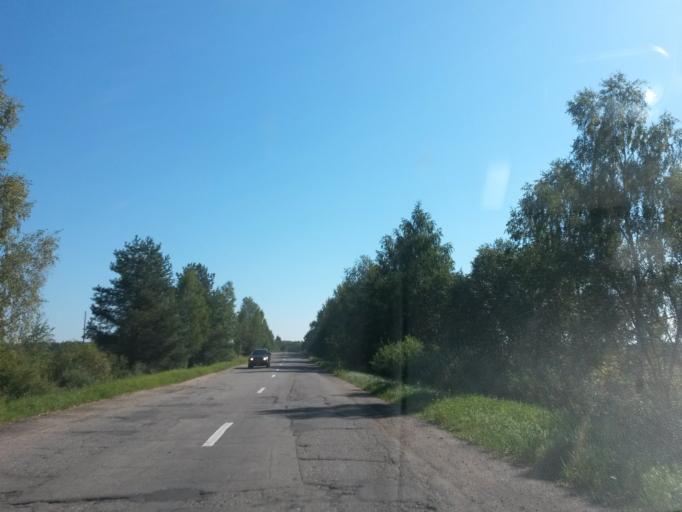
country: RU
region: Jaroslavl
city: Gavrilov-Yam
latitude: 57.3027
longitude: 40.0179
